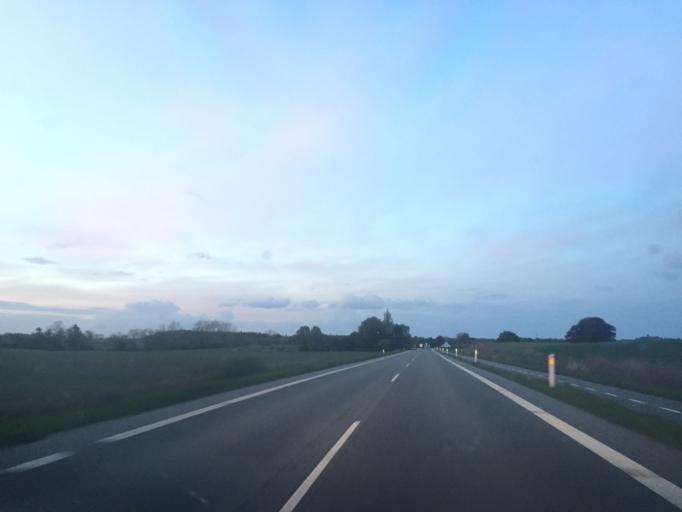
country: DK
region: South Denmark
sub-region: Nyborg Kommune
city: Nyborg
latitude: 55.3004
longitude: 10.7191
